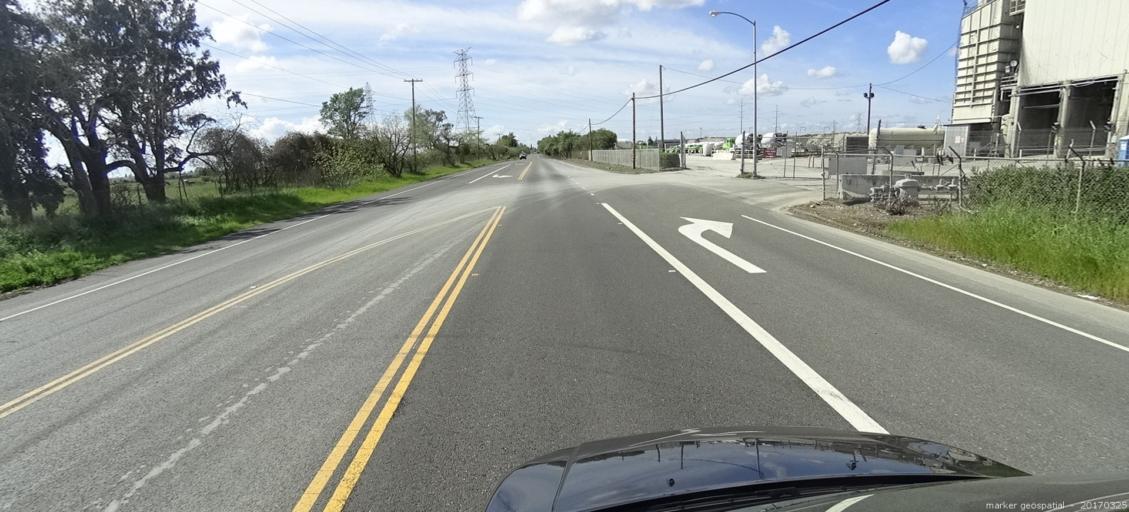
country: US
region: California
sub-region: Sacramento County
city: Rosemont
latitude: 38.5421
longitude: -121.3825
